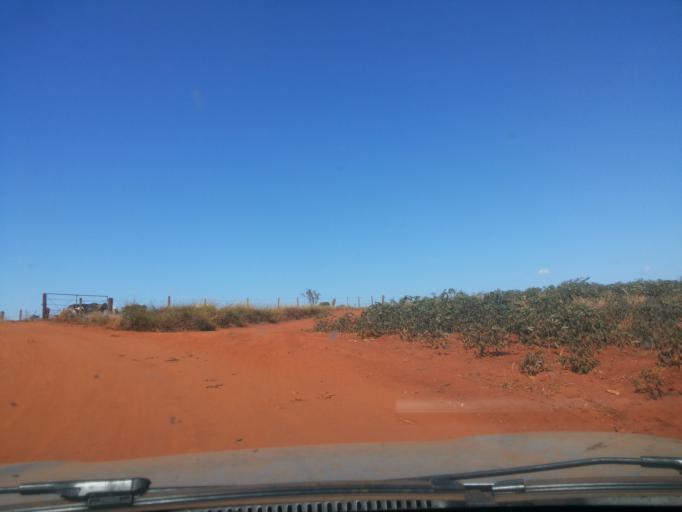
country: BR
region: Minas Gerais
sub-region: Centralina
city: Centralina
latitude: -18.7402
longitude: -49.1927
